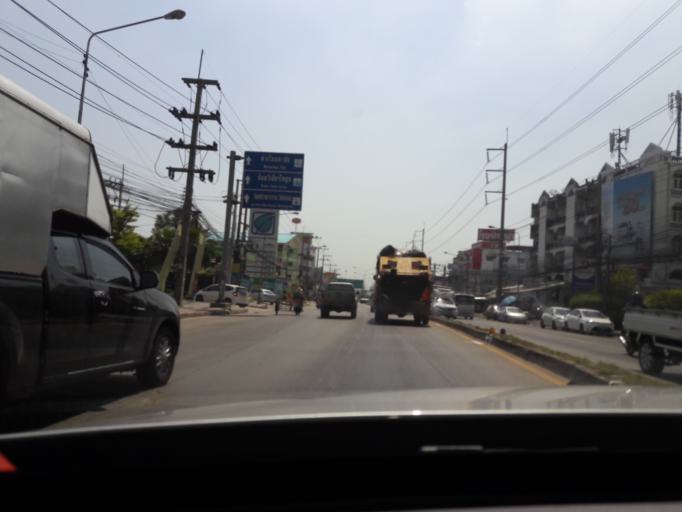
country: TH
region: Samut Sakhon
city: Samut Sakhon
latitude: 13.5681
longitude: 100.2719
